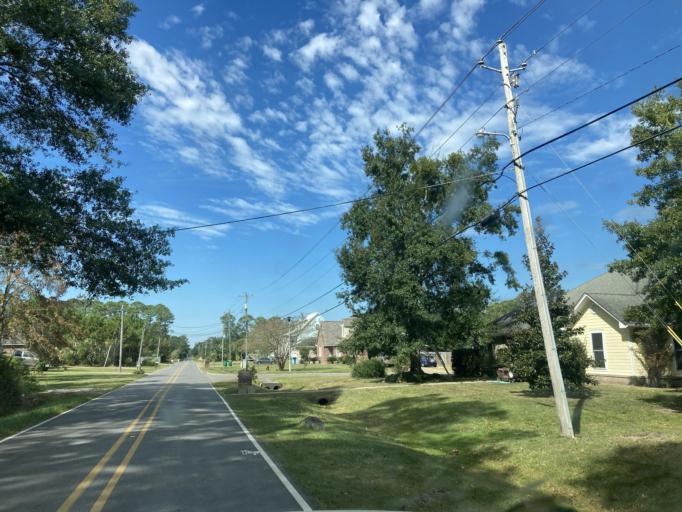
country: US
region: Mississippi
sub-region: Jackson County
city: Saint Martin
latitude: 30.4357
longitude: -88.8598
